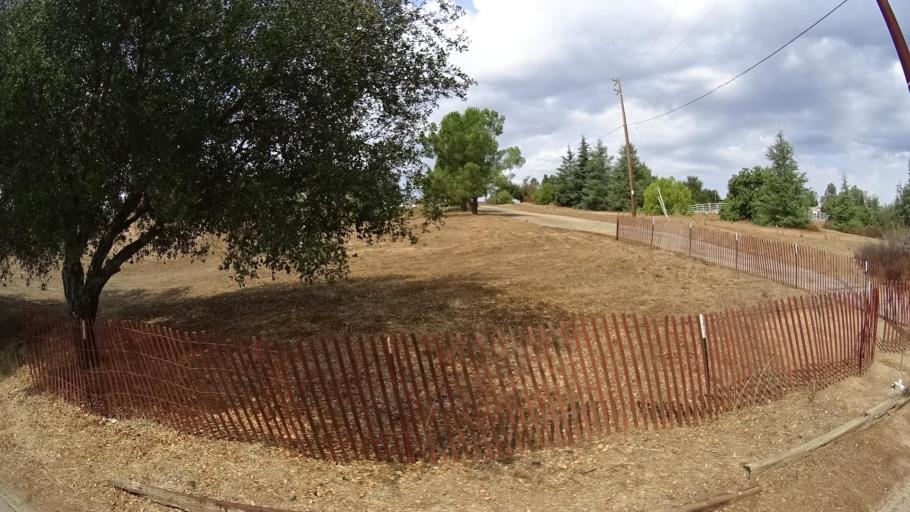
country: US
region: California
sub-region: San Diego County
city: Ramona
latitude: 33.0829
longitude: -116.8380
